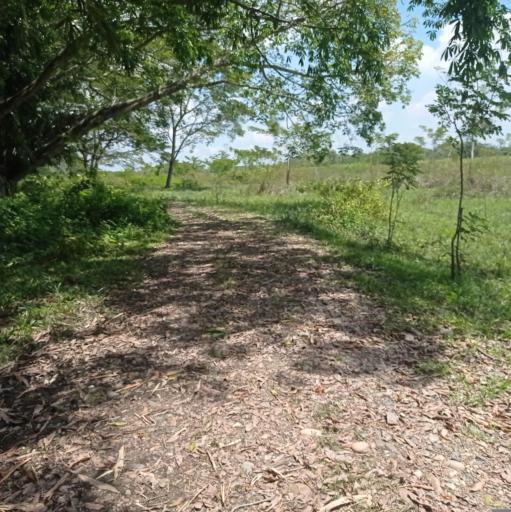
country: CO
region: Santander
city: Barrancabermeja
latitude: 7.0995
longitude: -73.8784
